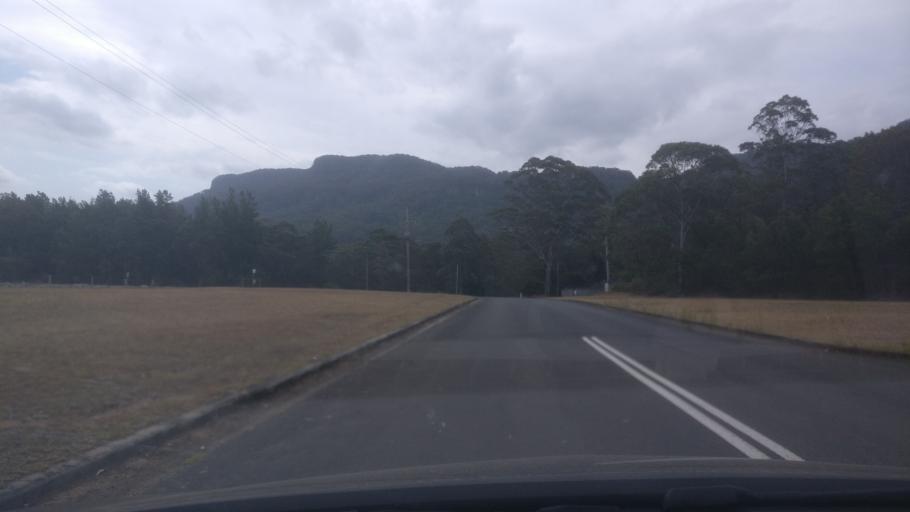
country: AU
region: New South Wales
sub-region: Shoalhaven Shire
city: Kangaroo Valley
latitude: -34.7234
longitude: 150.4788
